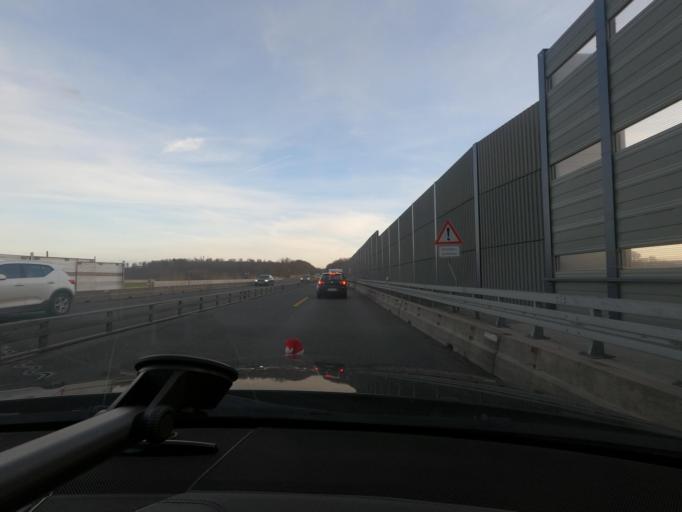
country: DE
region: Lower Saxony
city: Holle
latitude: 52.0992
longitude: 10.1544
